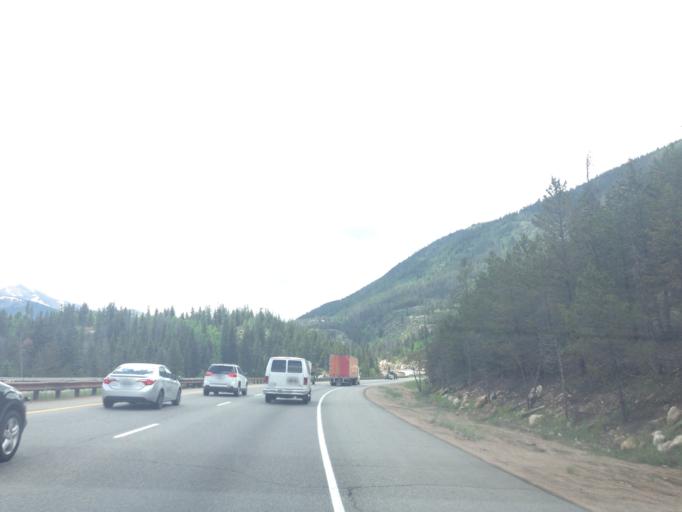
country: US
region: Colorado
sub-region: Clear Creek County
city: Georgetown
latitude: 39.6945
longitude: -105.7865
